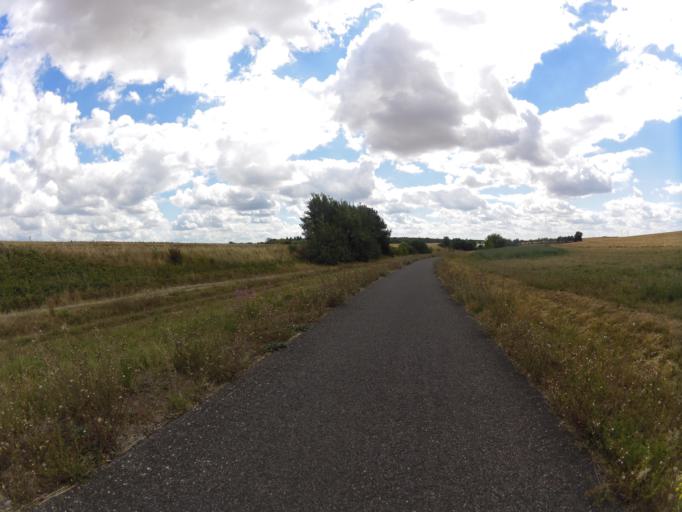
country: DE
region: Bavaria
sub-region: Regierungsbezirk Unterfranken
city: Aub
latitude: 49.5572
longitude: 10.0551
